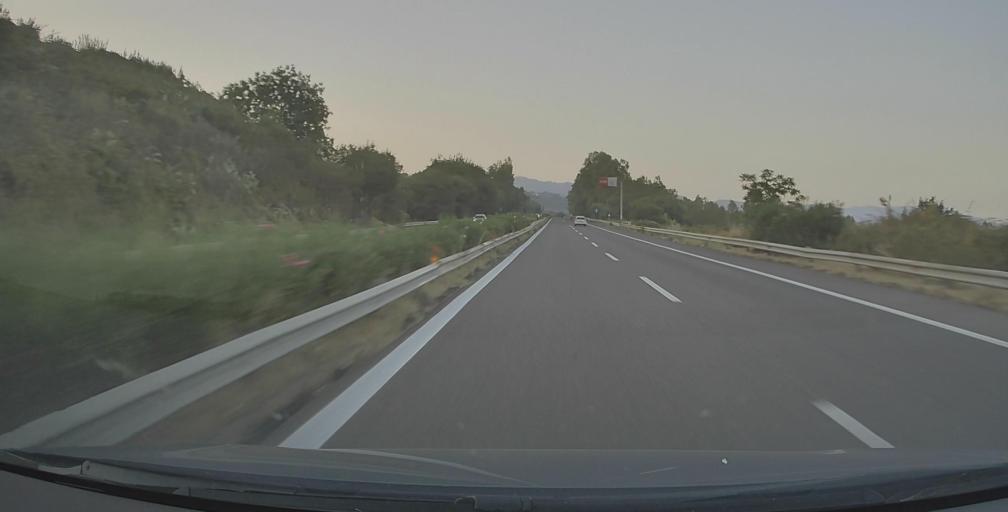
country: IT
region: Sicily
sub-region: Catania
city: Nunziata
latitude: 37.7750
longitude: 15.1839
